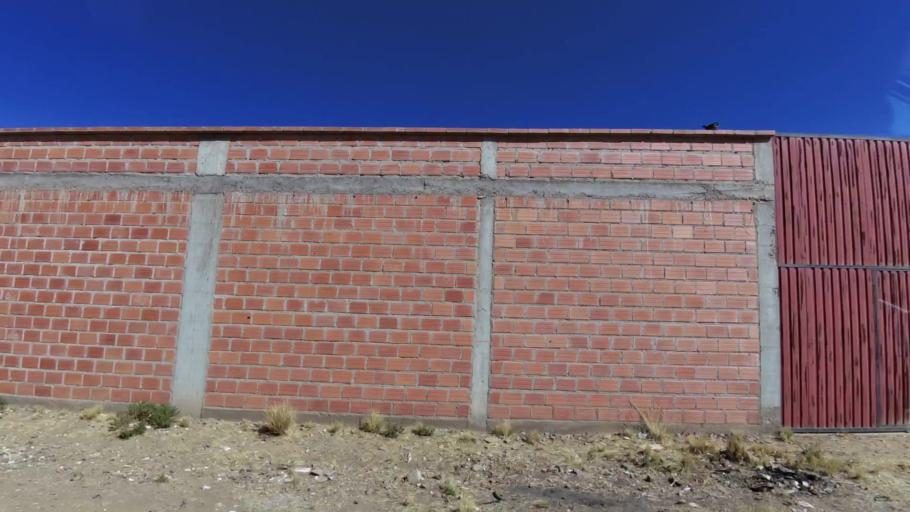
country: BO
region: La Paz
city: La Paz
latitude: -16.6191
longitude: -68.1944
